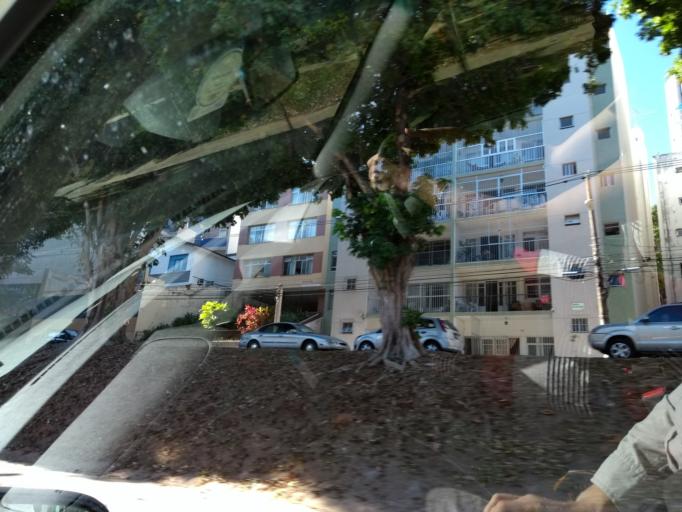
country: BR
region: Bahia
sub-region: Salvador
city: Salvador
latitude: -13.0005
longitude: -38.5194
